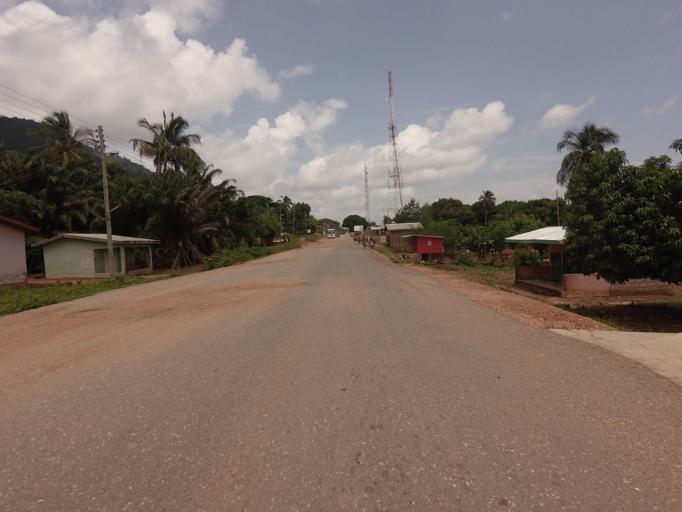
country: GH
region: Volta
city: Ho
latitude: 6.7592
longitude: 0.3613
